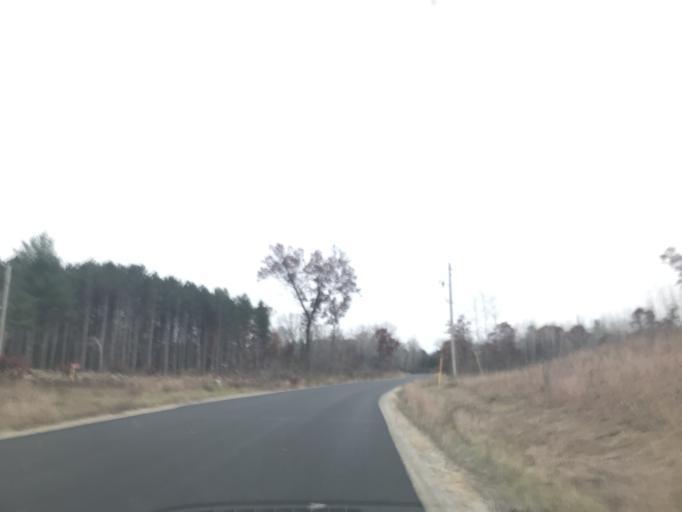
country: US
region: Wisconsin
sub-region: Marinette County
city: Peshtigo
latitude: 45.1296
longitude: -87.7508
